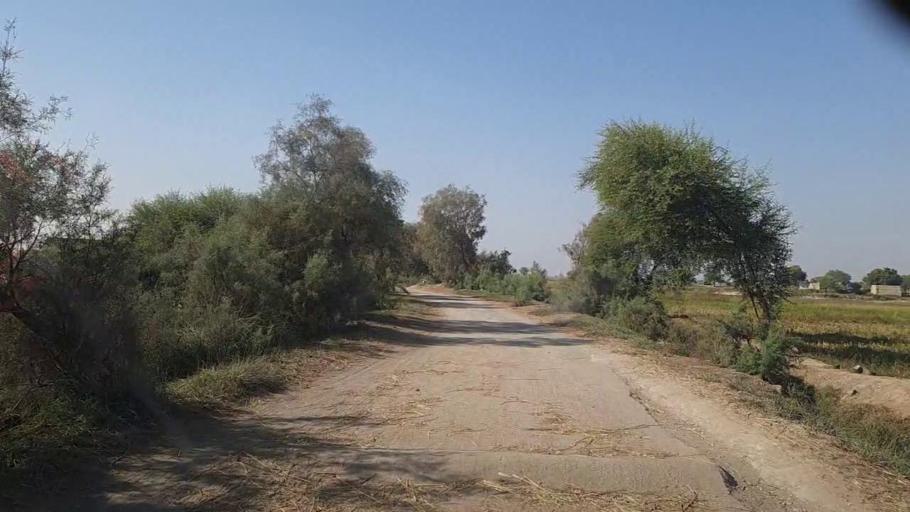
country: PK
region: Sindh
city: Tangwani
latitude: 28.2499
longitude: 68.9420
